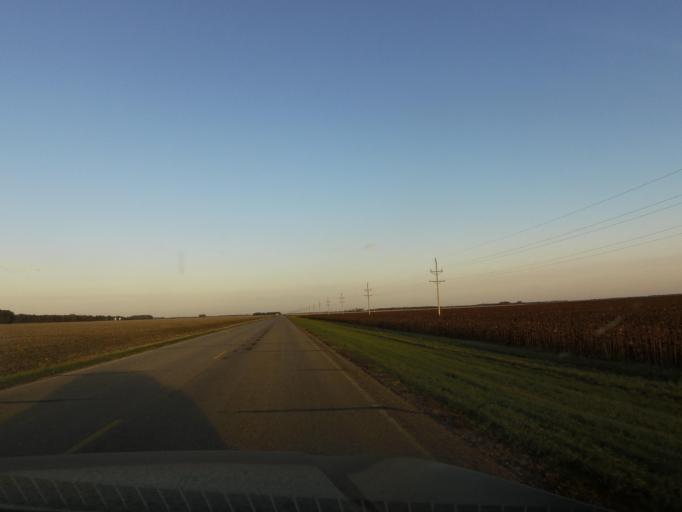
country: CA
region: Manitoba
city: Altona
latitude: 48.9633
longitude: -97.6335
